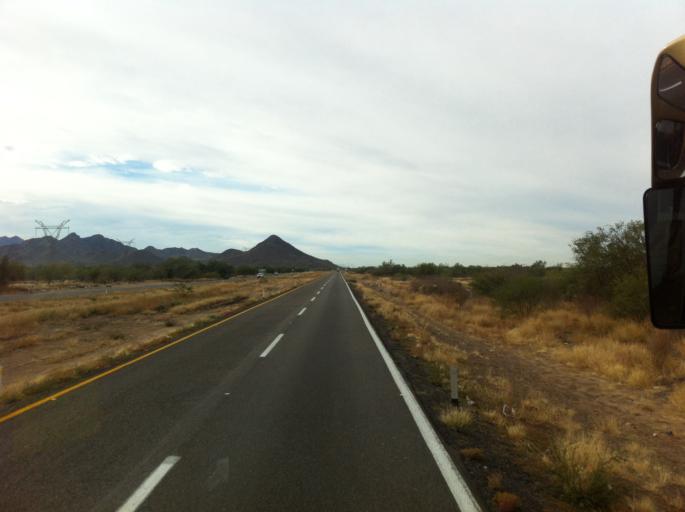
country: MX
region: Sonora
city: Hermosillo
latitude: 28.6767
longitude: -110.9938
